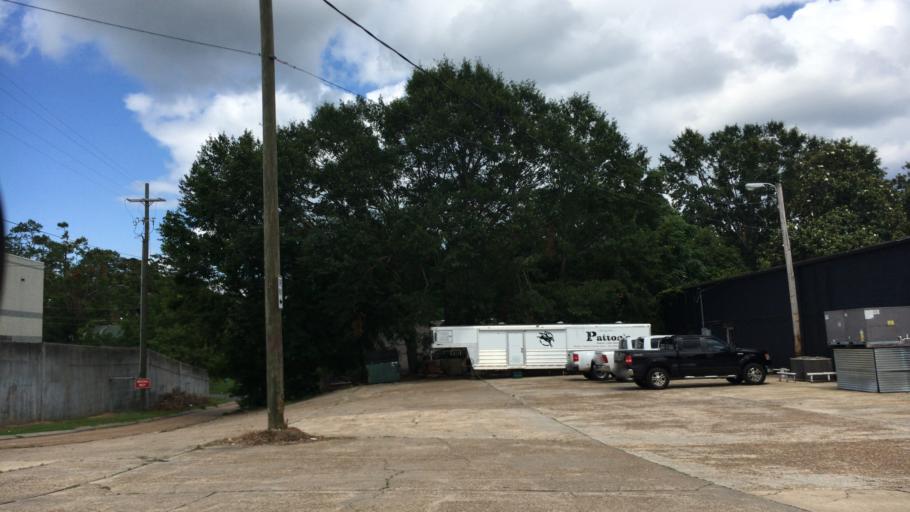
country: US
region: Louisiana
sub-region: Lincoln Parish
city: Ruston
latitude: 32.5366
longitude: -92.6388
